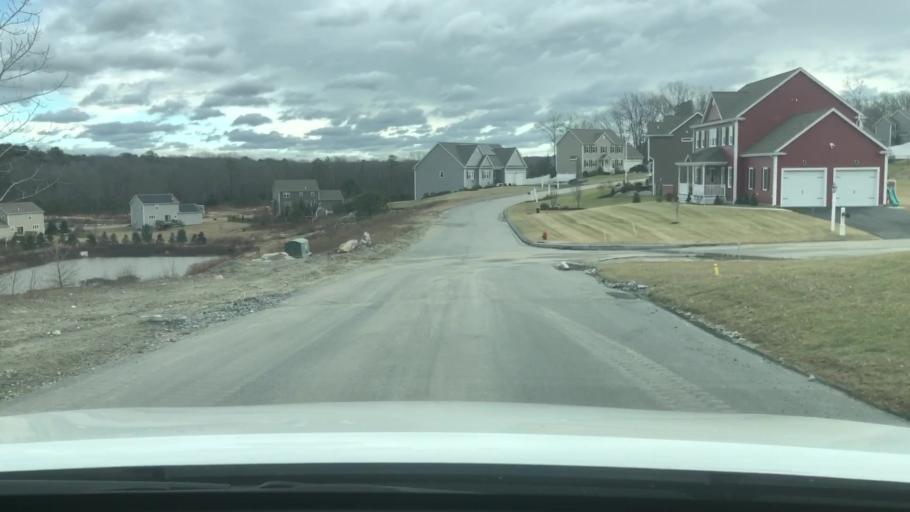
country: US
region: Rhode Island
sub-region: Providence County
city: Woonsocket
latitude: 42.0359
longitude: -71.5122
